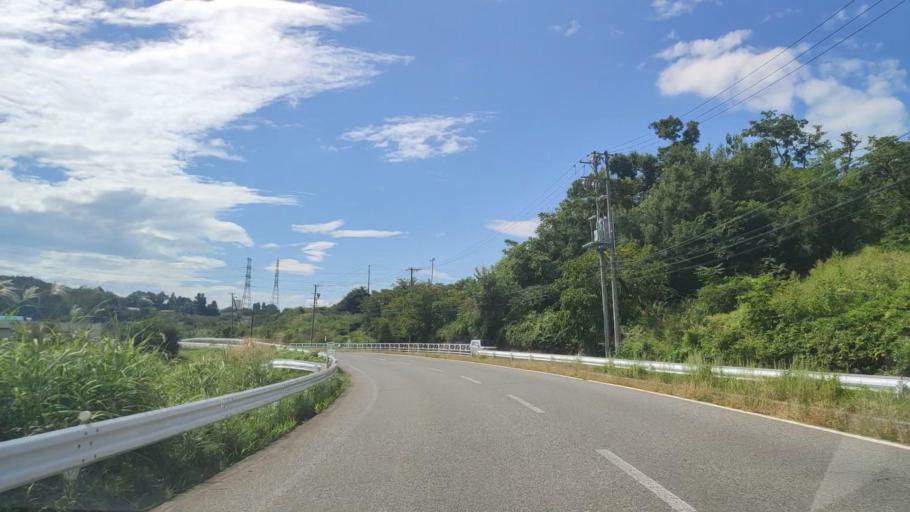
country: JP
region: Nagano
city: Nakano
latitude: 36.7407
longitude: 138.3060
